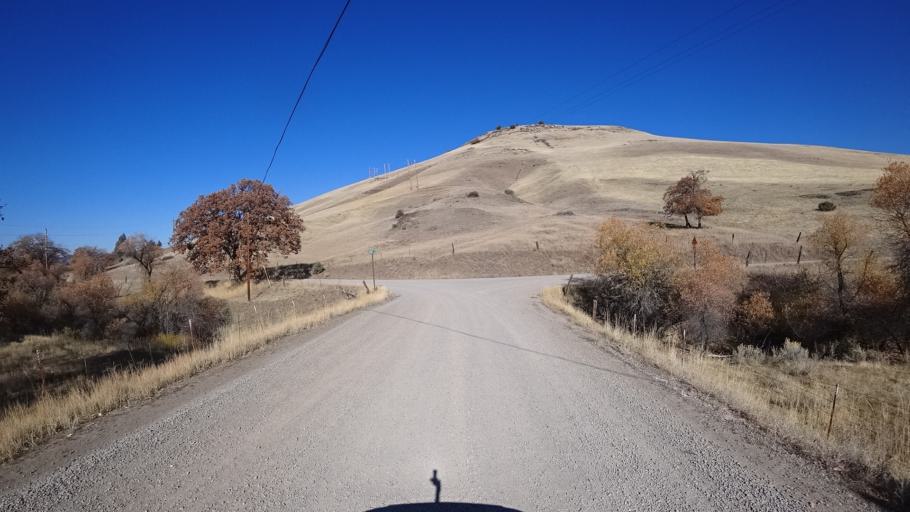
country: US
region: California
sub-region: Siskiyou County
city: Montague
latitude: 41.7931
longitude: -122.3609
